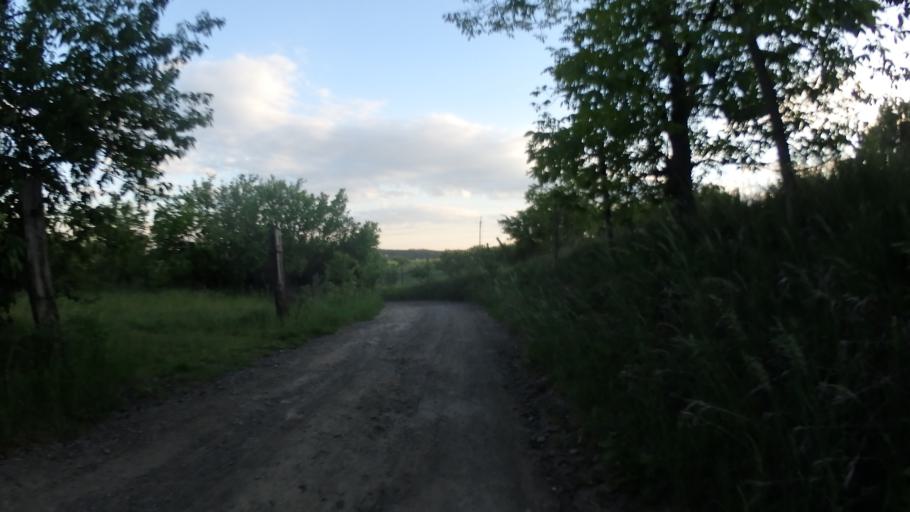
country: CZ
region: South Moravian
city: Modrice
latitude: 49.1251
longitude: 16.5963
